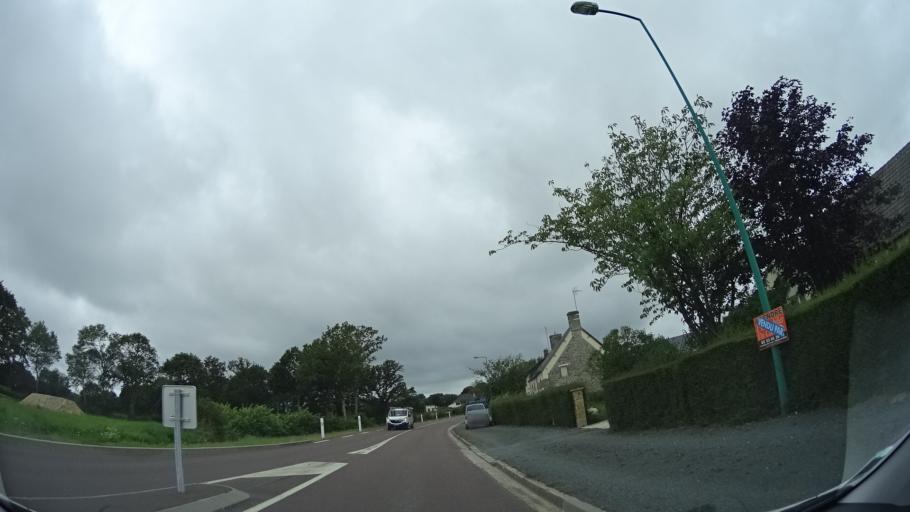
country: FR
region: Lower Normandy
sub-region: Departement de la Manche
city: La Haye-du-Puits
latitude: 49.3016
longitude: -1.5797
